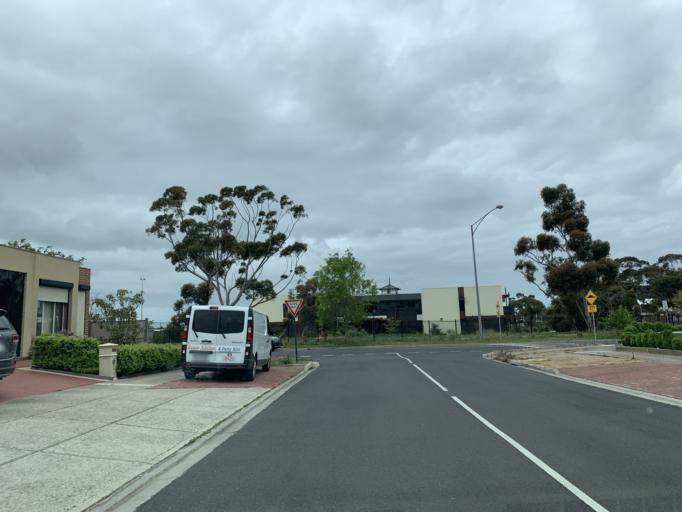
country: AU
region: Victoria
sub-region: Brimbank
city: Cairnlea
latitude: -37.7548
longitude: 144.7924
